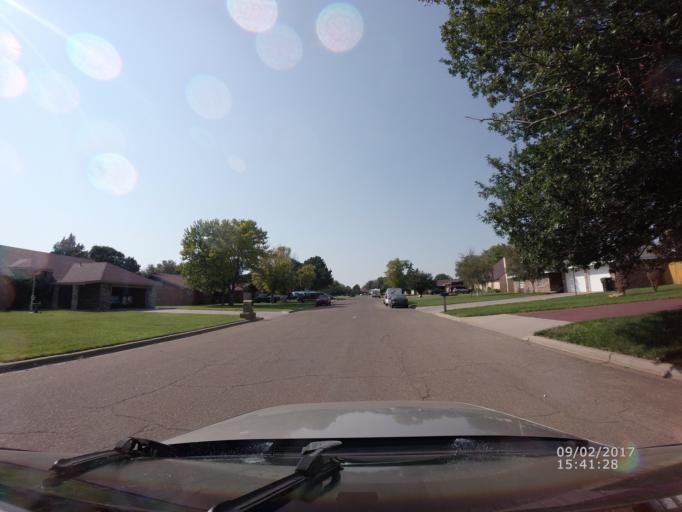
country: US
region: New Mexico
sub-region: Curry County
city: Clovis
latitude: 34.4424
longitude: -103.1895
